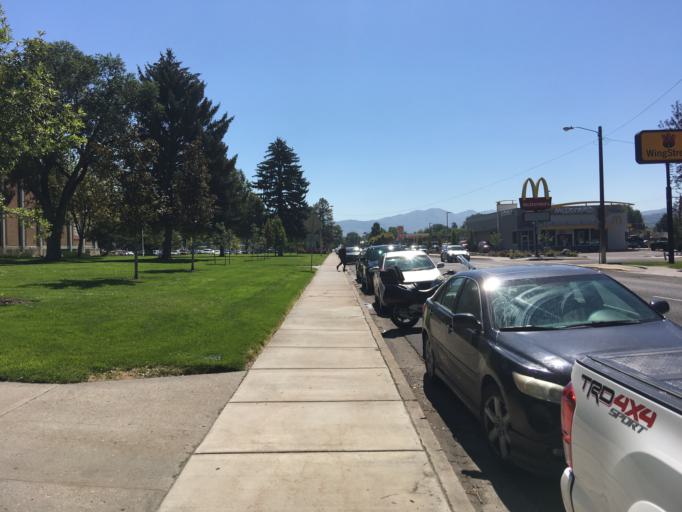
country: US
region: Idaho
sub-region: Bannock County
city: Pocatello
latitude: 42.8602
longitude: -112.4360
